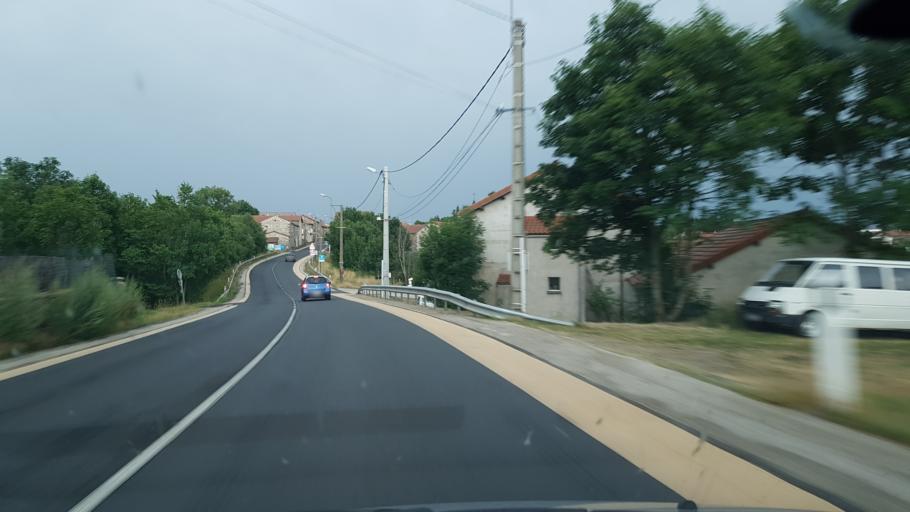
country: FR
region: Auvergne
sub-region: Departement de la Haute-Loire
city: Allegre
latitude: 45.1460
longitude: 3.6650
